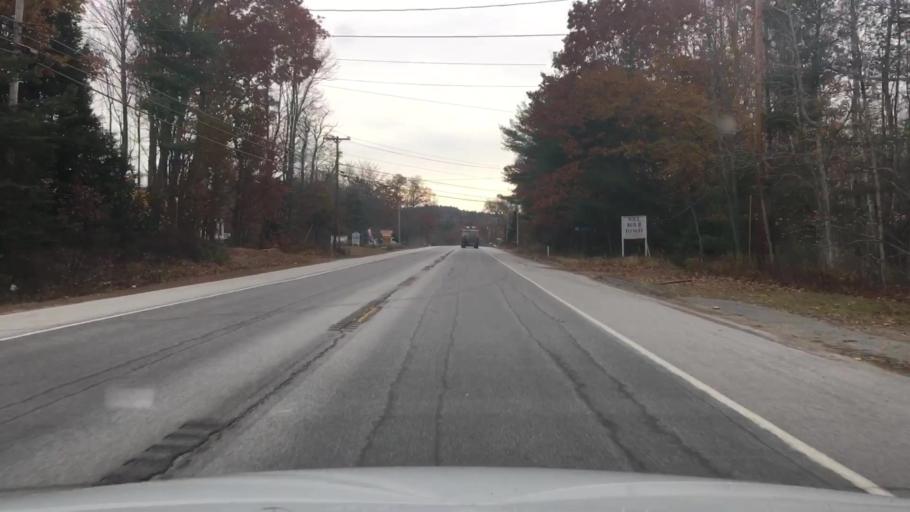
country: US
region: Maine
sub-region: Hancock County
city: Orland
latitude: 44.5651
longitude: -68.7166
